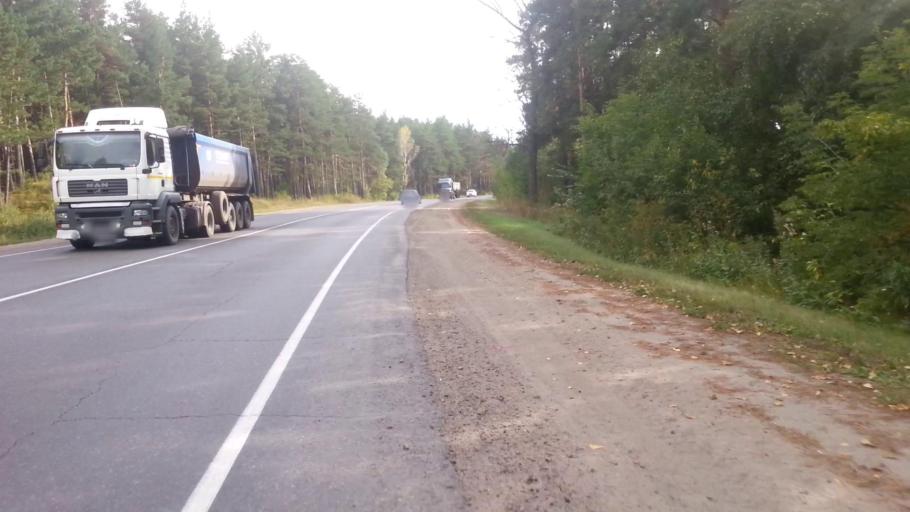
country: RU
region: Altai Krai
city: Yuzhnyy
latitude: 53.3036
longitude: 83.7040
